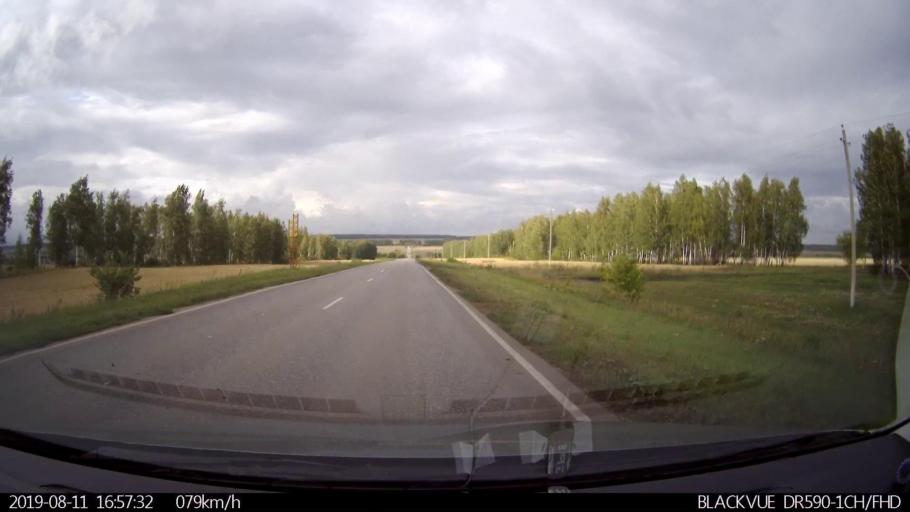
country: RU
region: Ulyanovsk
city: Mayna
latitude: 54.2989
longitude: 47.6534
